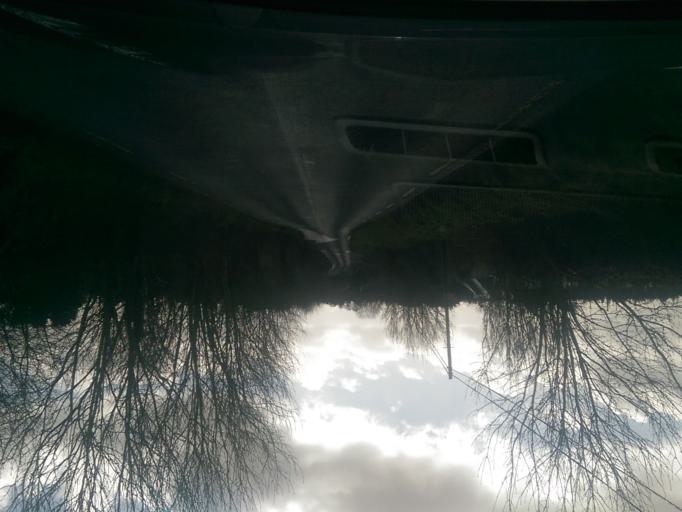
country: IE
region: Connaught
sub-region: County Galway
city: Athenry
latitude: 53.3807
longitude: -8.6955
